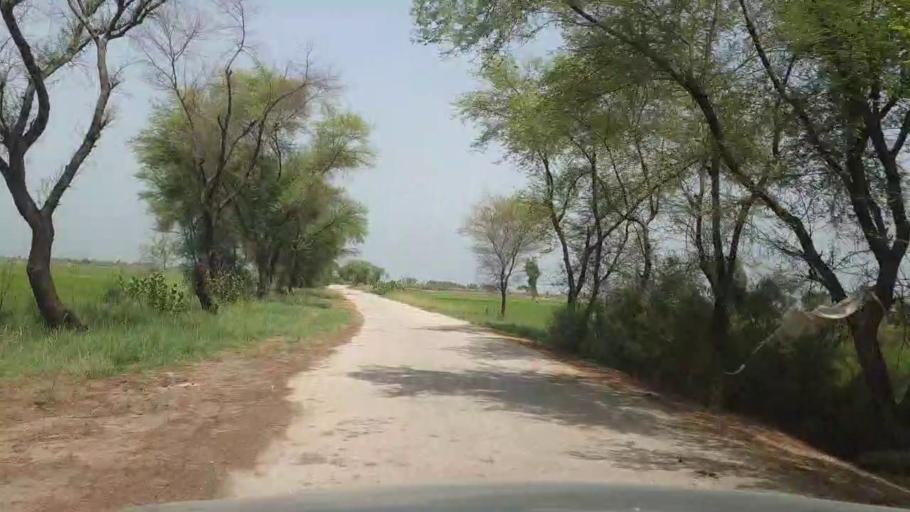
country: PK
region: Sindh
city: Garhi Yasin
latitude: 27.9488
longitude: 68.3675
